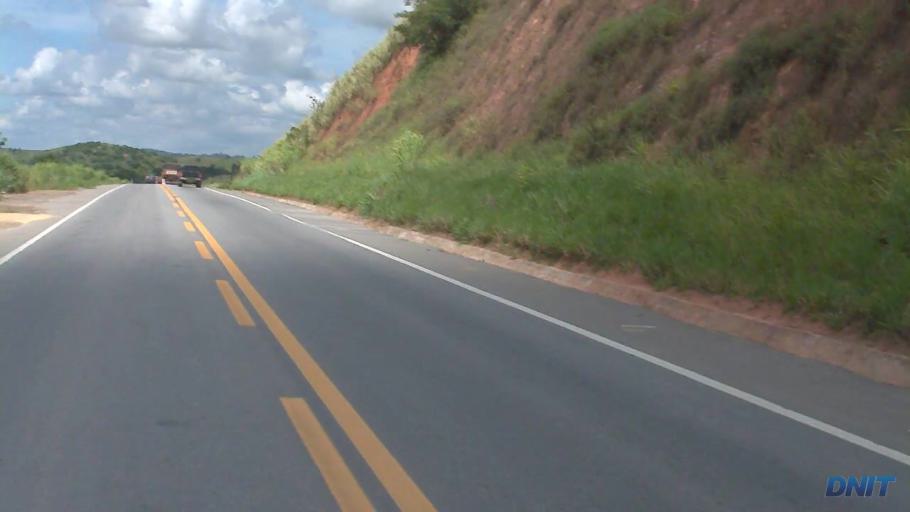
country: BR
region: Minas Gerais
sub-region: Governador Valadares
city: Governador Valadares
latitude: -18.9844
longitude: -42.1069
